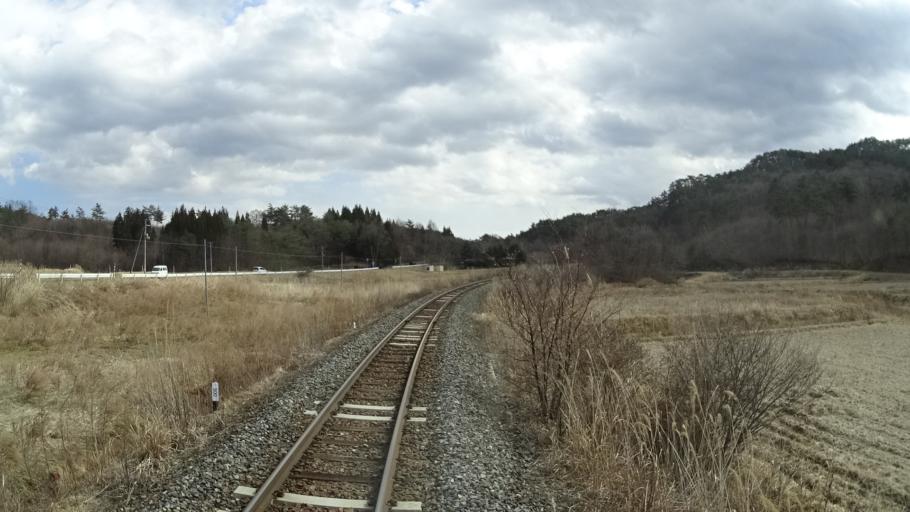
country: JP
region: Iwate
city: Tono
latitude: 39.3298
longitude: 141.3639
